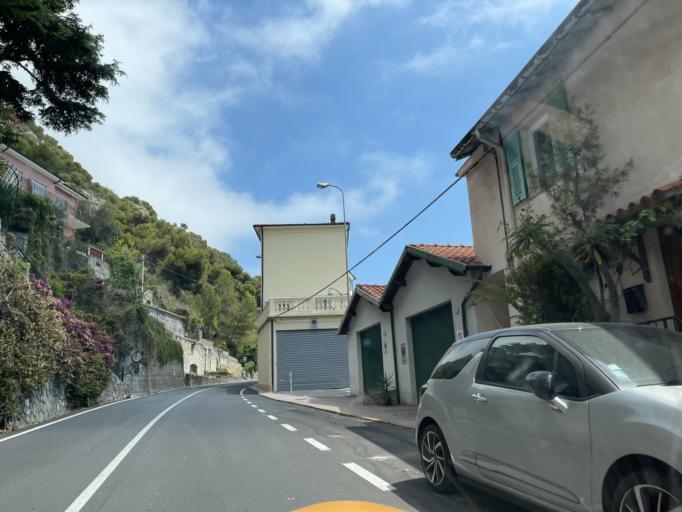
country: FR
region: Provence-Alpes-Cote d'Azur
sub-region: Departement des Alpes-Maritimes
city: Menton
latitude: 43.7866
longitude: 7.5428
